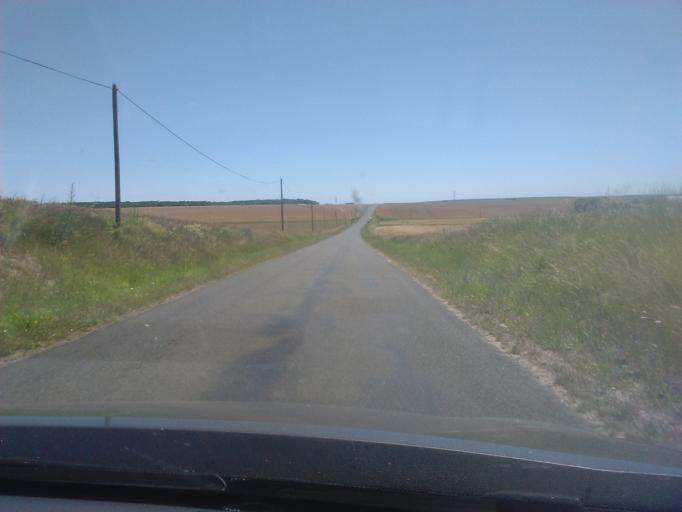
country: FR
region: Centre
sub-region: Departement du Loir-et-Cher
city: Herbault
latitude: 47.6430
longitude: 1.1941
